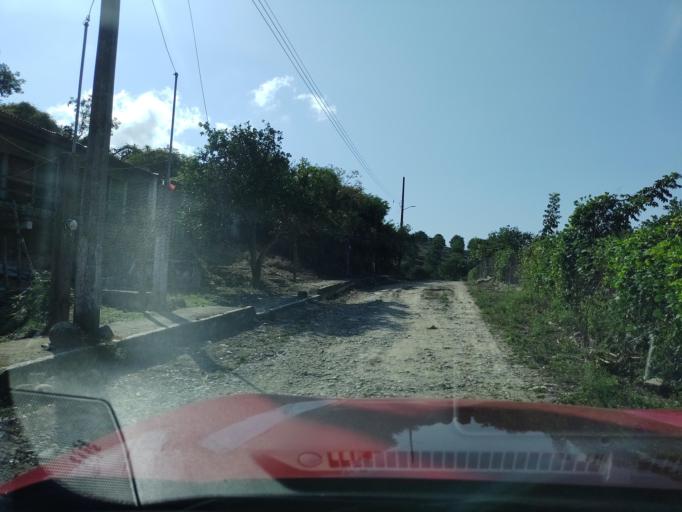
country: MX
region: Veracruz
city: Agua Dulce
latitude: 20.2867
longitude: -97.1858
